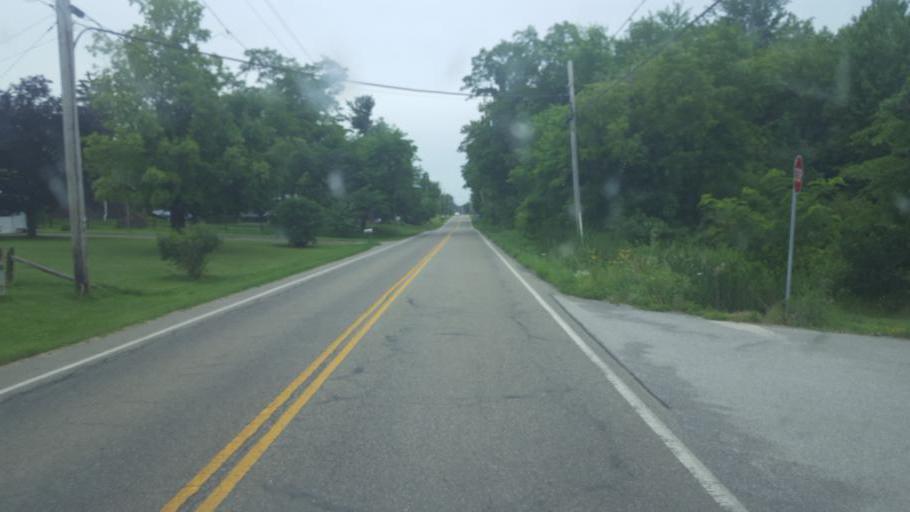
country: US
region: Ohio
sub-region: Trumbull County
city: Cortland
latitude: 41.3405
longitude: -80.7315
